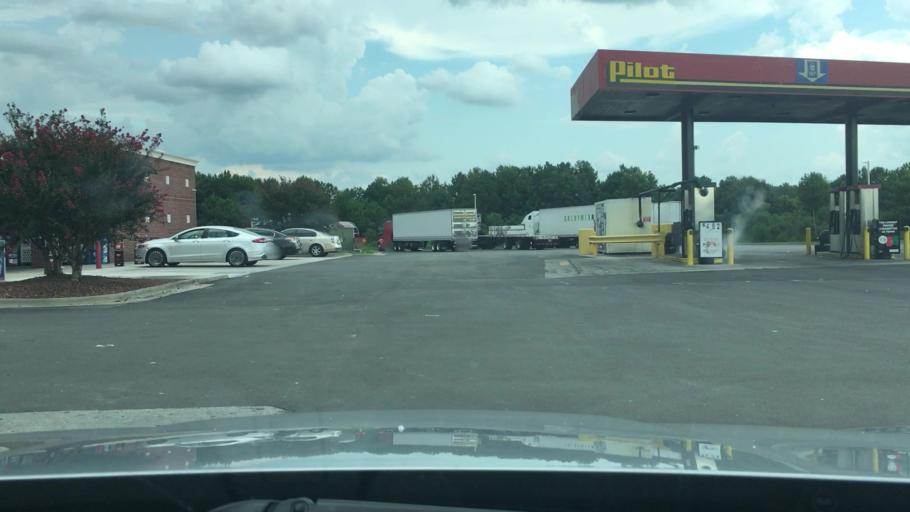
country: US
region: North Carolina
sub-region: Harnett County
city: Dunn
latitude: 35.2698
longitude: -78.6153
